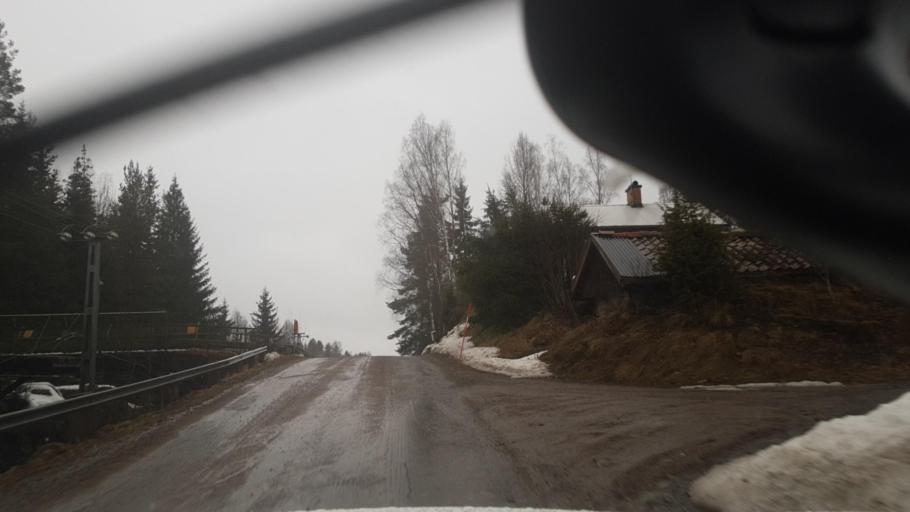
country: SE
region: Vaermland
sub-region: Eda Kommun
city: Amotfors
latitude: 59.8235
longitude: 12.3641
